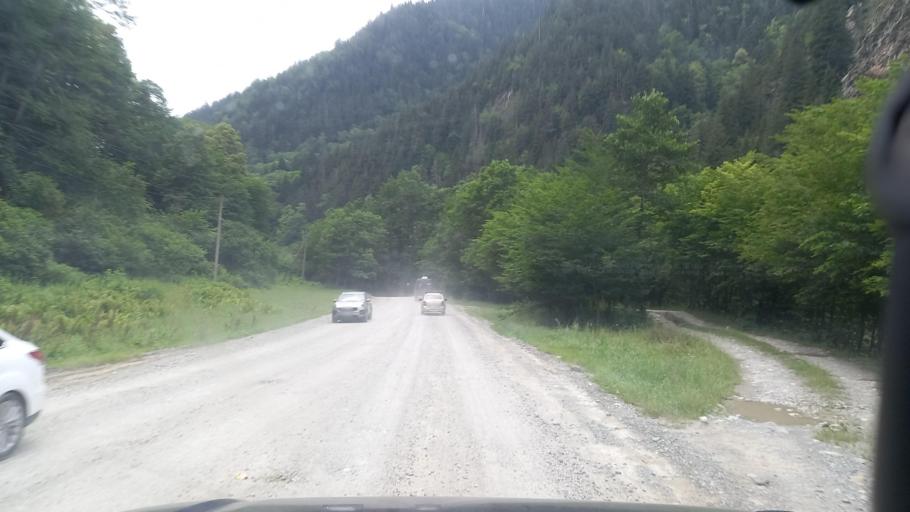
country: RU
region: Karachayevo-Cherkesiya
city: Kurdzhinovo
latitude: 43.8862
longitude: 40.9497
